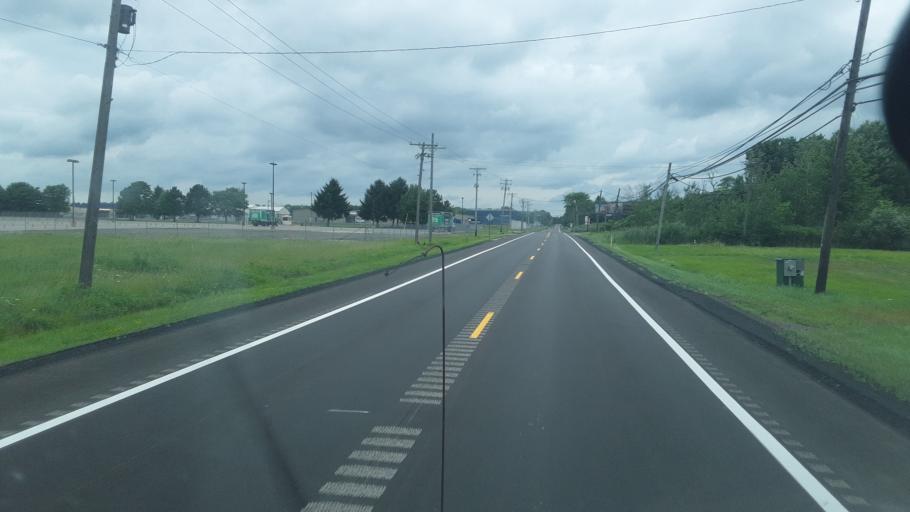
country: US
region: Ohio
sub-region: Trumbull County
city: Howland Center
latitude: 41.2555
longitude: -80.6638
